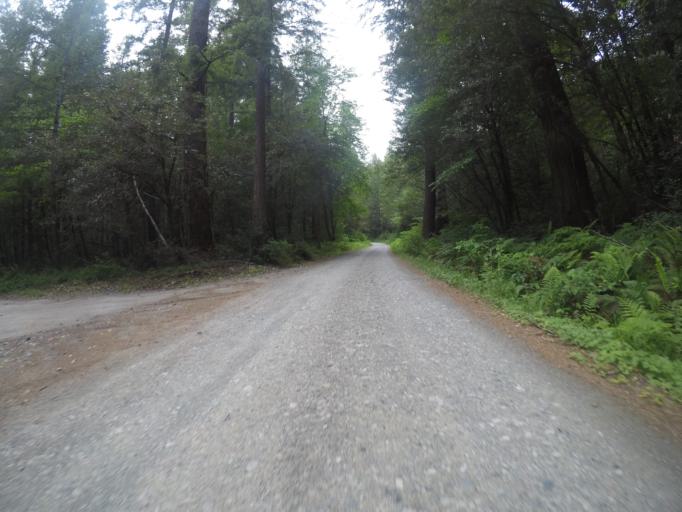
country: US
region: California
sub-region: Del Norte County
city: Bertsch-Oceanview
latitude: 41.6872
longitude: -123.9082
